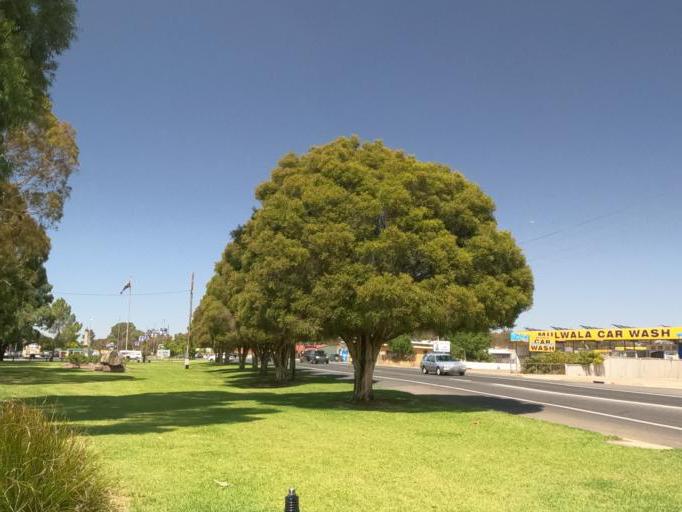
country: AU
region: New South Wales
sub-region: Corowa Shire
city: Mulwala
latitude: -35.9927
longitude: 146.0023
